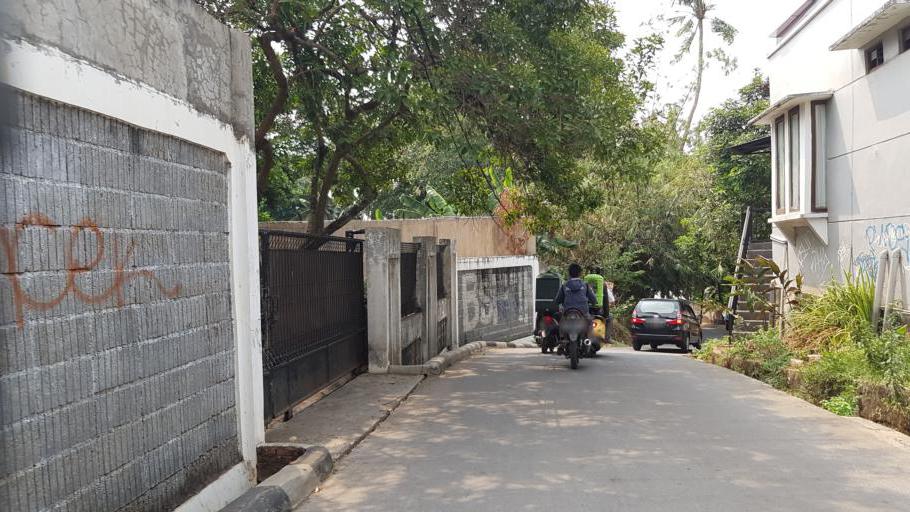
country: ID
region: West Java
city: Pamulang
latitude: -6.3302
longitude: 106.7920
